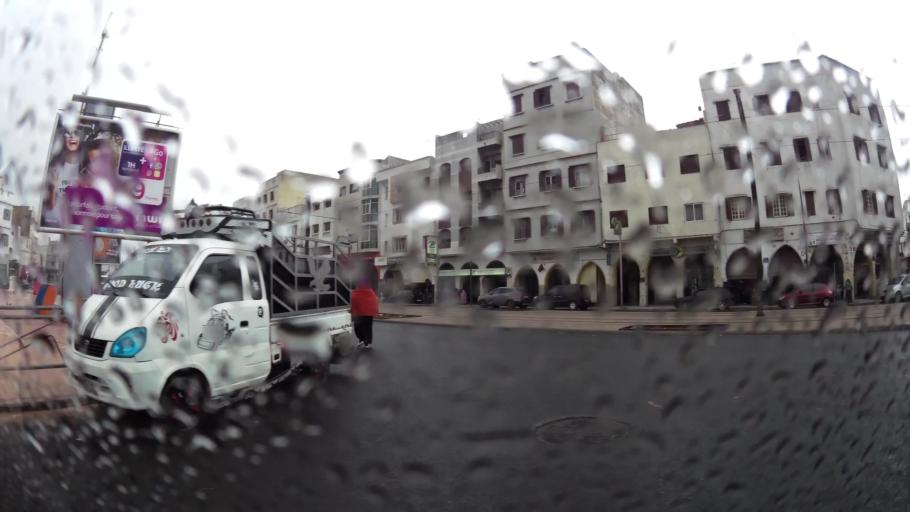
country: MA
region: Grand Casablanca
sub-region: Casablanca
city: Casablanca
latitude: 33.5694
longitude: -7.6030
